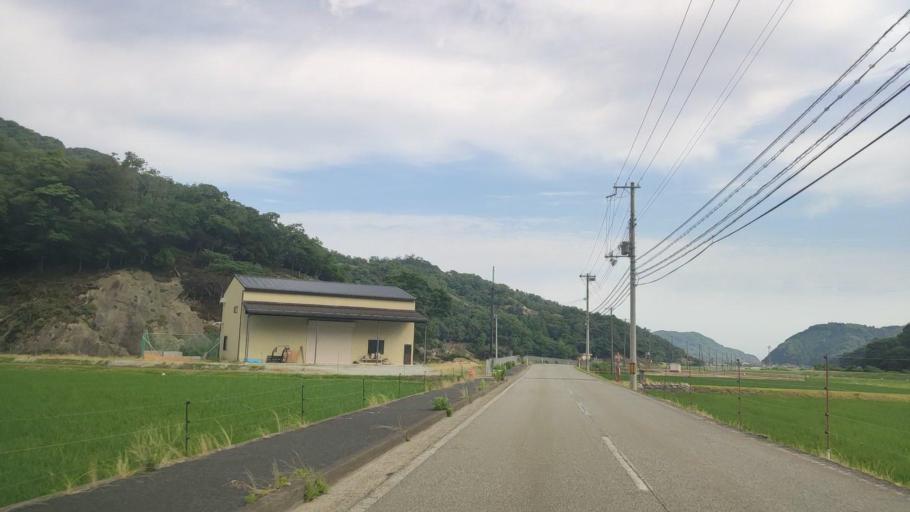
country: JP
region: Hyogo
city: Toyooka
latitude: 35.6201
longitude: 134.8418
